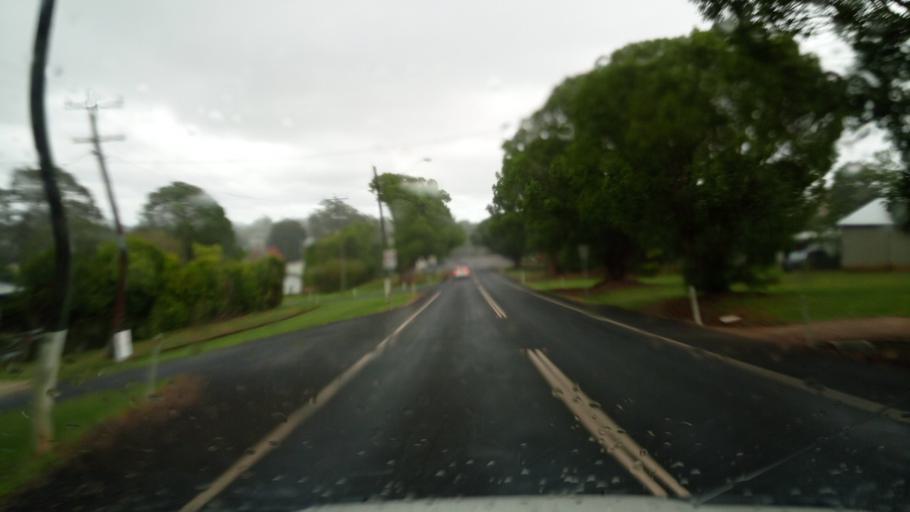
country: AU
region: Queensland
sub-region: Tablelands
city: Tolga
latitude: -17.2729
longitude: 145.5850
